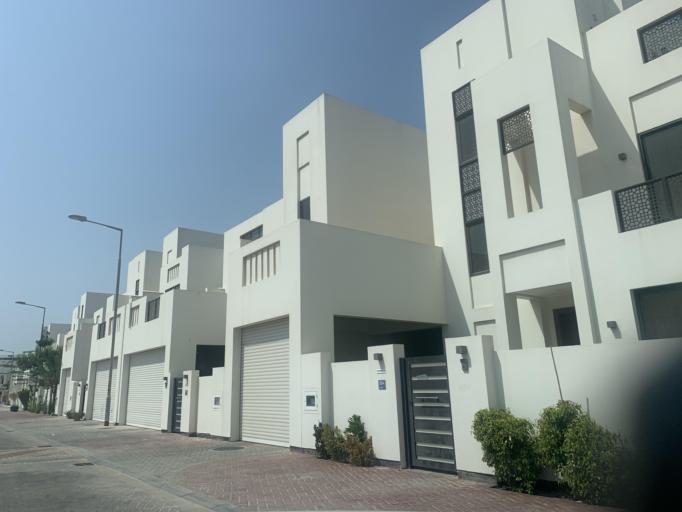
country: BH
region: Muharraq
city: Al Muharraq
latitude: 26.3005
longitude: 50.6361
